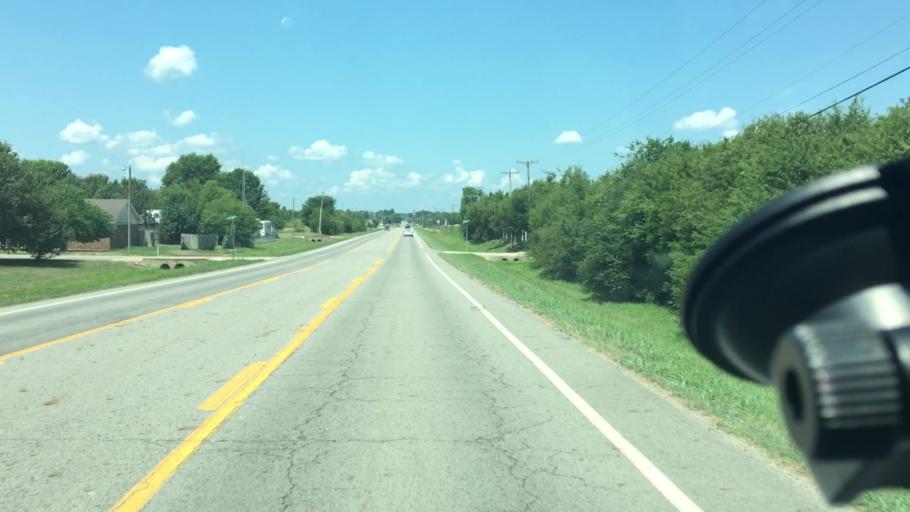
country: US
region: Arkansas
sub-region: Franklin County
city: Charleston
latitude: 35.2968
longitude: -94.0159
